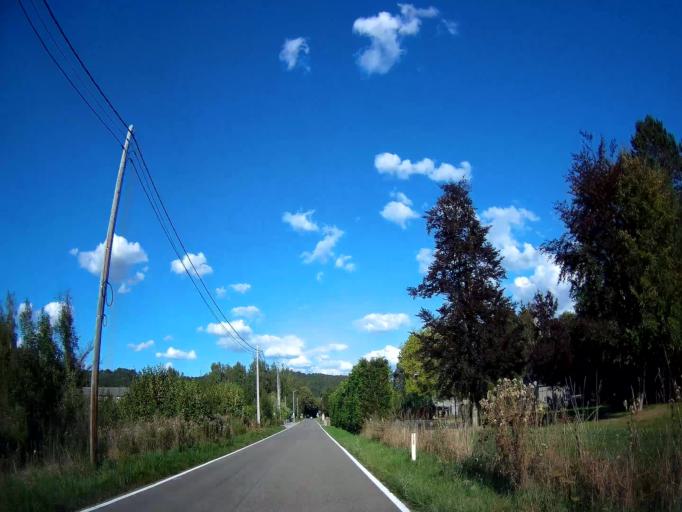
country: BE
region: Wallonia
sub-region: Province de Namur
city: Anhee
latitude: 50.3159
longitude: 4.8391
